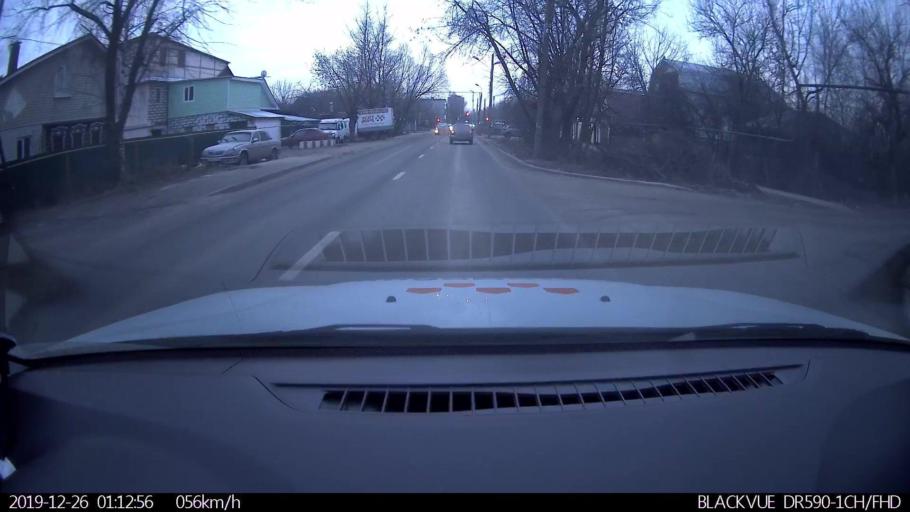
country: RU
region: Nizjnij Novgorod
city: Nizhniy Novgorod
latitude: 56.2807
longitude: 43.9131
